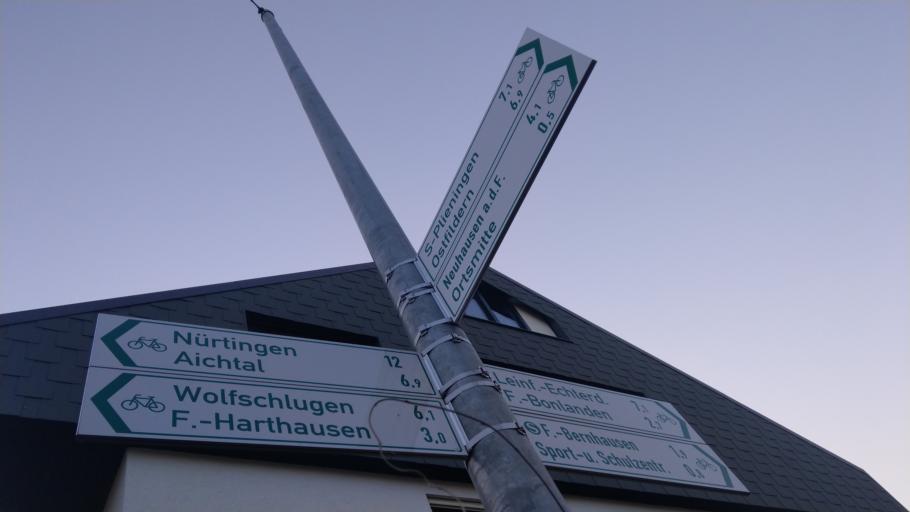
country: DE
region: Baden-Wuerttemberg
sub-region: Regierungsbezirk Stuttgart
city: Filderstadt
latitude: 48.6703
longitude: 9.2342
